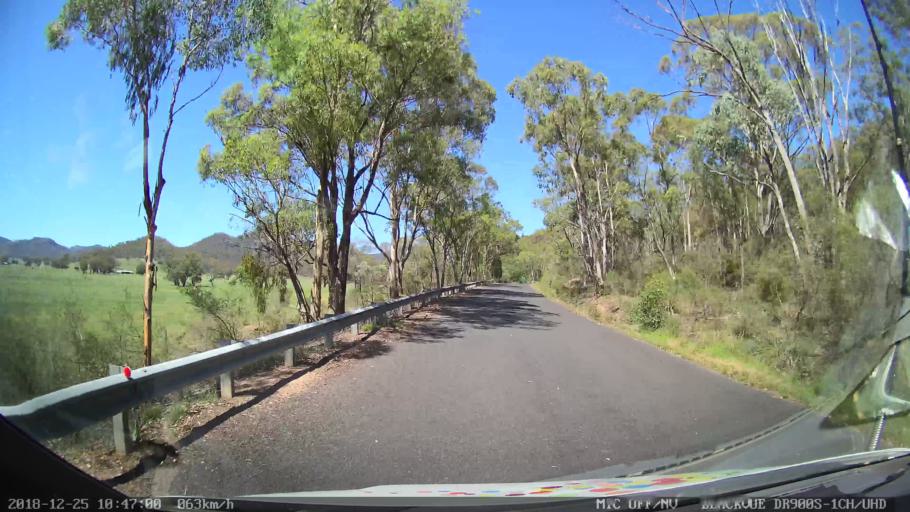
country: AU
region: New South Wales
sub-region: Upper Hunter Shire
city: Merriwa
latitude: -32.4454
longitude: 150.2800
